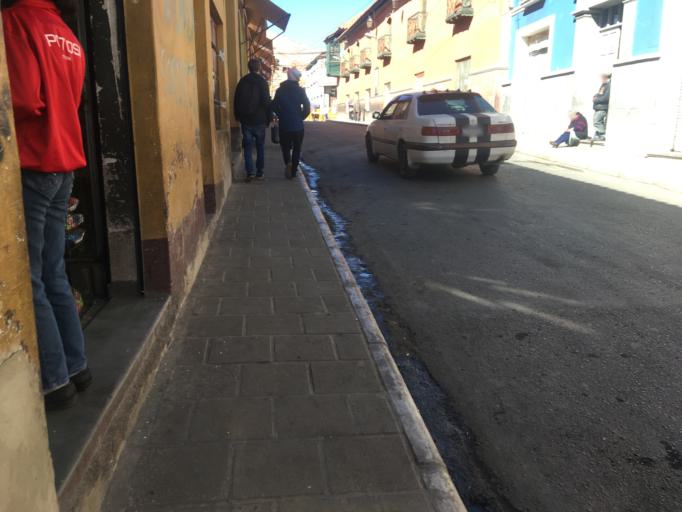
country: BO
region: Potosi
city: Potosi
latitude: -19.5871
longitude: -65.7555
